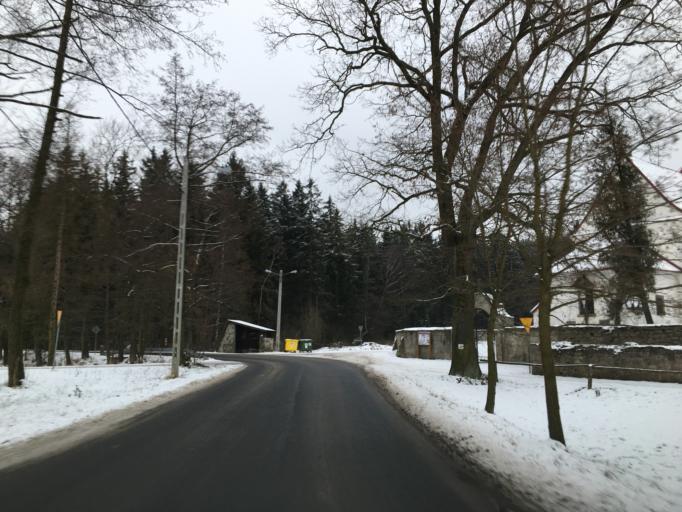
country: PL
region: Lower Silesian Voivodeship
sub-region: Powiat walbrzyski
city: Mieroszow
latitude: 50.6871
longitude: 16.1535
